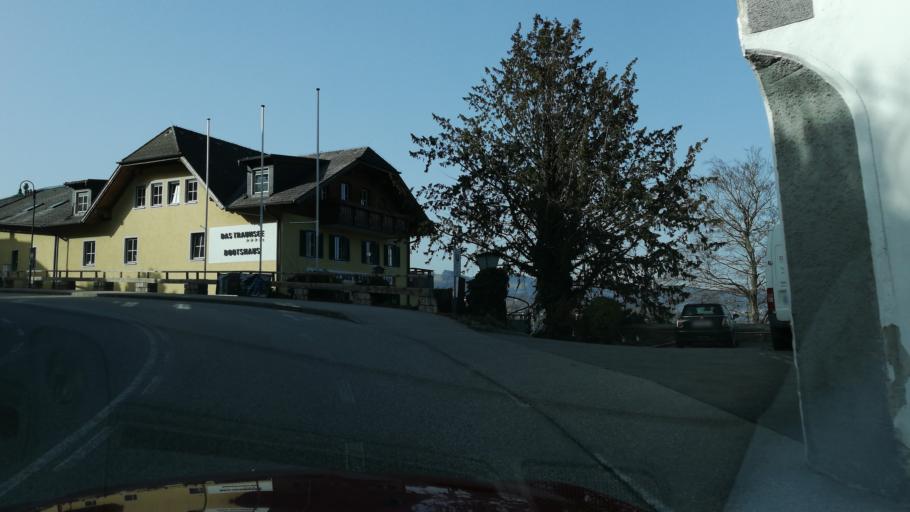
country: AT
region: Upper Austria
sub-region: Politischer Bezirk Gmunden
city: Ebensee
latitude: 47.8457
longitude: 13.7906
